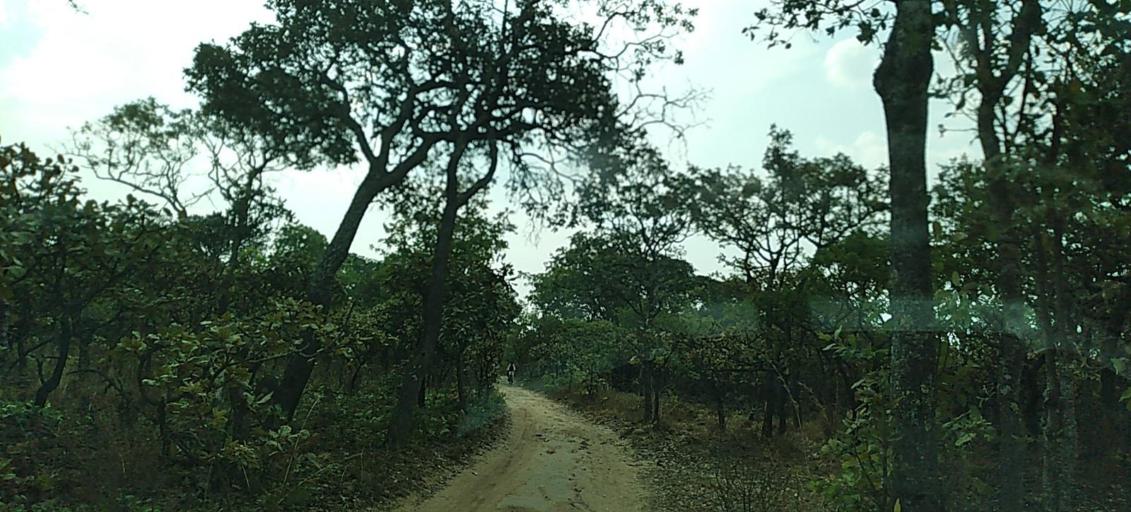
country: ZM
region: North-Western
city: Solwezi
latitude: -12.0759
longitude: 26.2385
